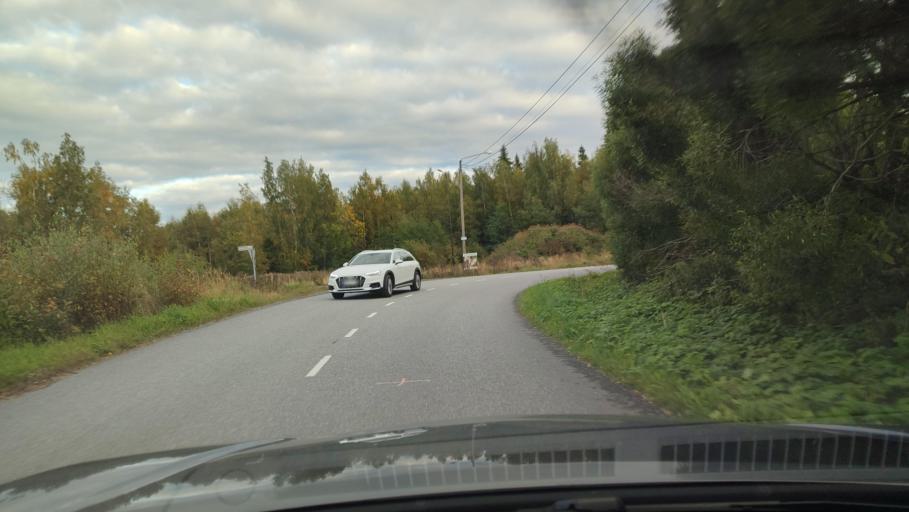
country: FI
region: Ostrobothnia
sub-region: Sydosterbotten
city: Kristinestad
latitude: 62.2625
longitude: 21.3848
